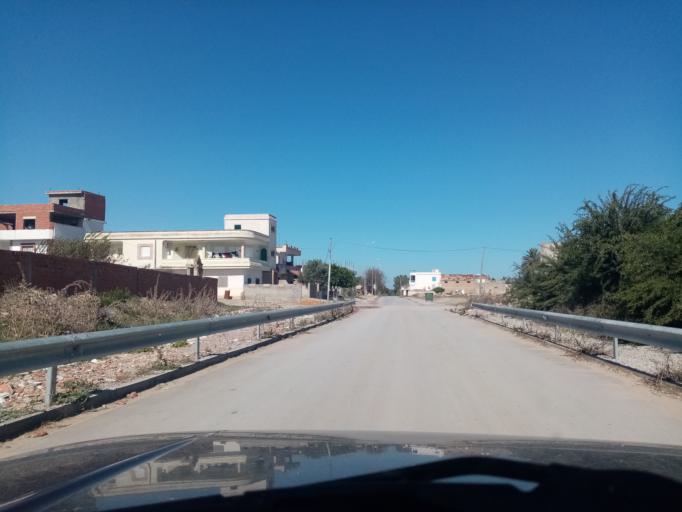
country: TN
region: Nabul
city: Bu `Urqub
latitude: 36.5804
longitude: 10.5695
